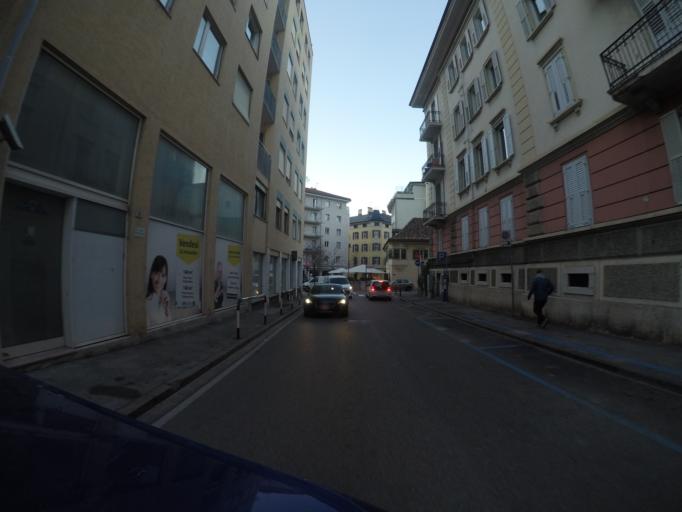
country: IT
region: Trentino-Alto Adige
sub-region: Bolzano
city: Bolzano
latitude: 46.5007
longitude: 11.3609
